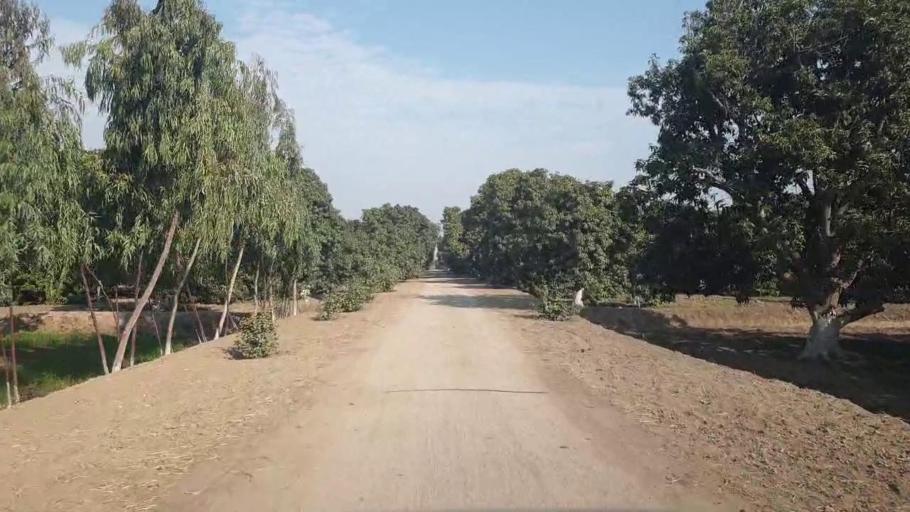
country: PK
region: Sindh
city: Tando Adam
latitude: 25.7534
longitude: 68.5882
